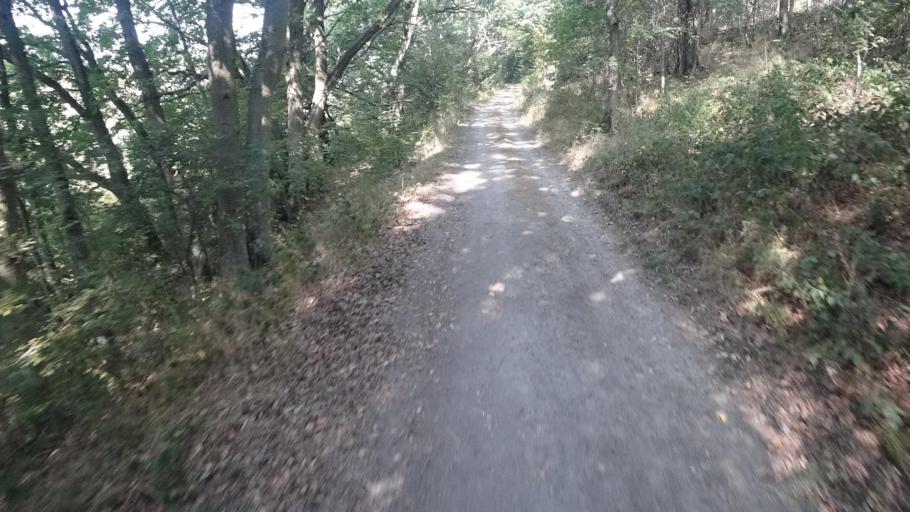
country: DE
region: Rheinland-Pfalz
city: Mutterschied
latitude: 49.9882
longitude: 7.5598
